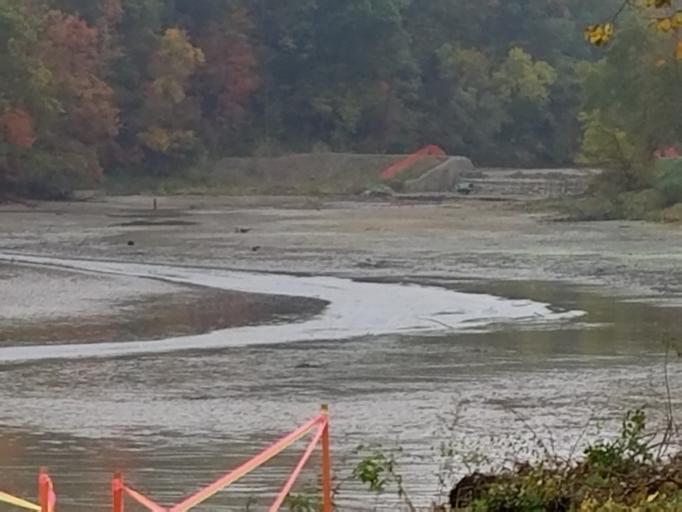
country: US
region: Ohio
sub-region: Morrow County
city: Mount Gilead
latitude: 40.5486
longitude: -82.8178
